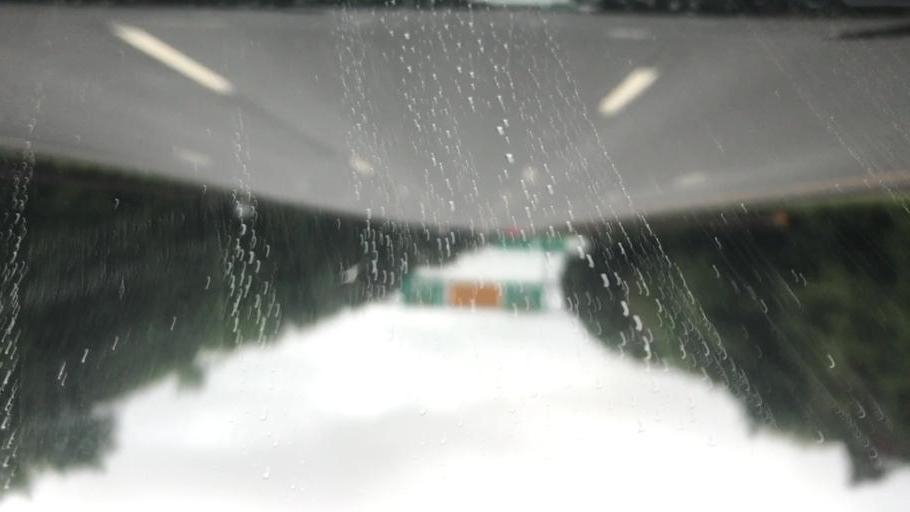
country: US
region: New Jersey
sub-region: Monmouth County
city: Wanamassa
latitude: 40.2446
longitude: -74.0837
